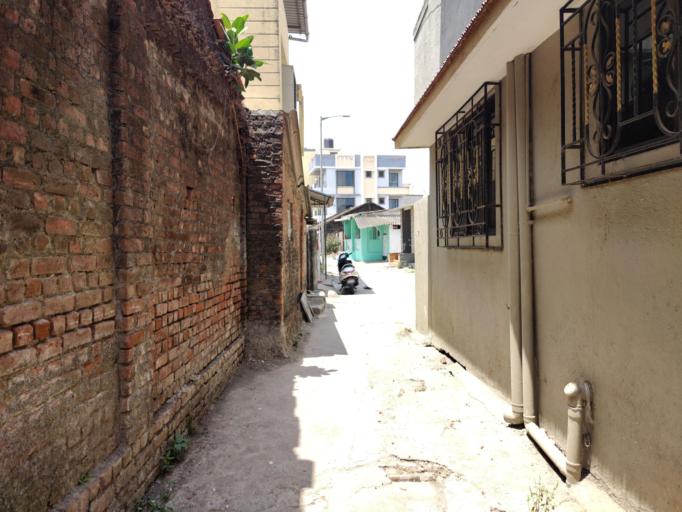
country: IN
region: Daman and Diu
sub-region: Daman District
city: Daman
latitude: 20.4051
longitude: 72.8296
